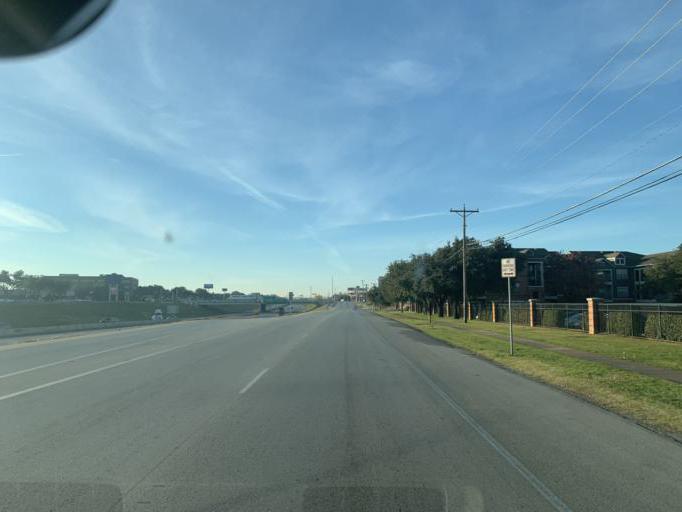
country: US
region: Texas
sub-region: Tarrant County
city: Euless
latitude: 32.7886
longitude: -97.0589
